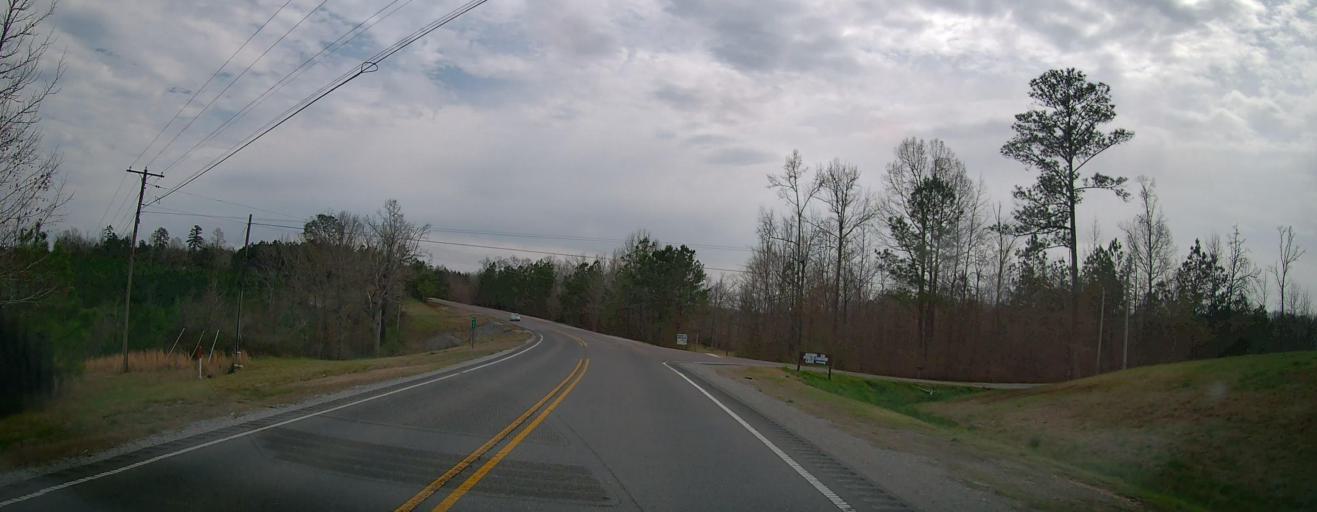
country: US
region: Alabama
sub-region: Marion County
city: Hamilton
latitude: 34.0510
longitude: -87.9652
